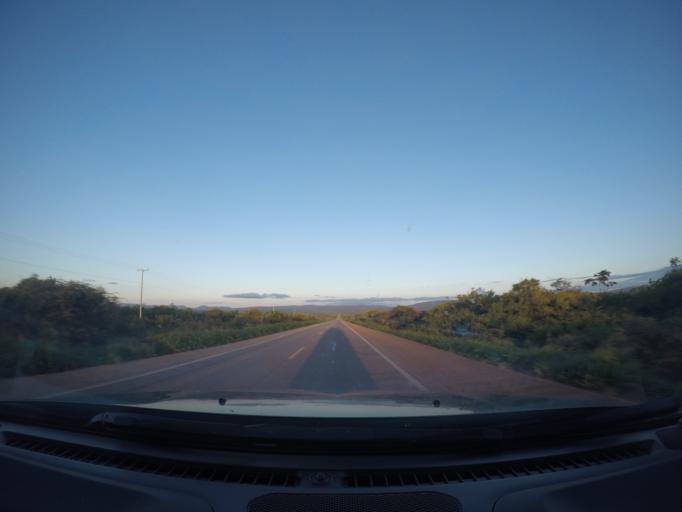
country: BR
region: Bahia
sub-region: Seabra
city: Seabra
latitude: -12.4082
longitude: -41.9641
